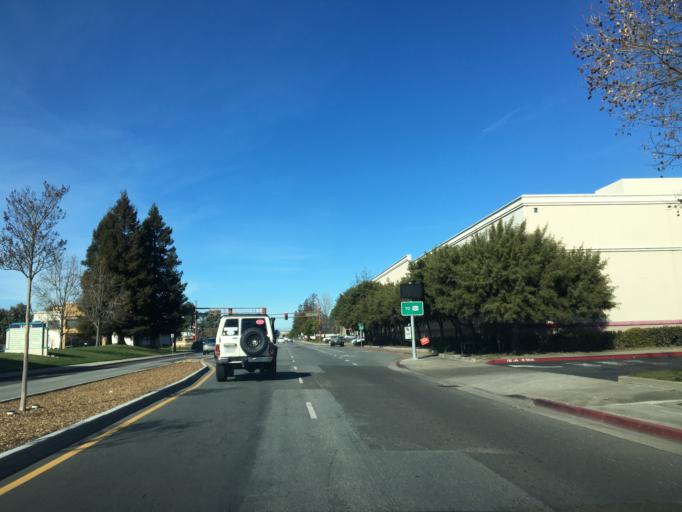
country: US
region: California
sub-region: San Mateo County
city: San Carlos
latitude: 37.5029
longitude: -122.2475
